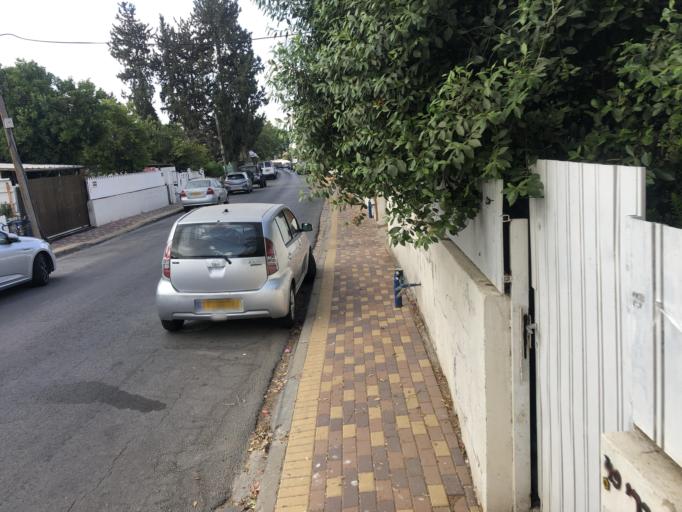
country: IL
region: Central District
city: Yehud
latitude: 32.0319
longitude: 34.8828
